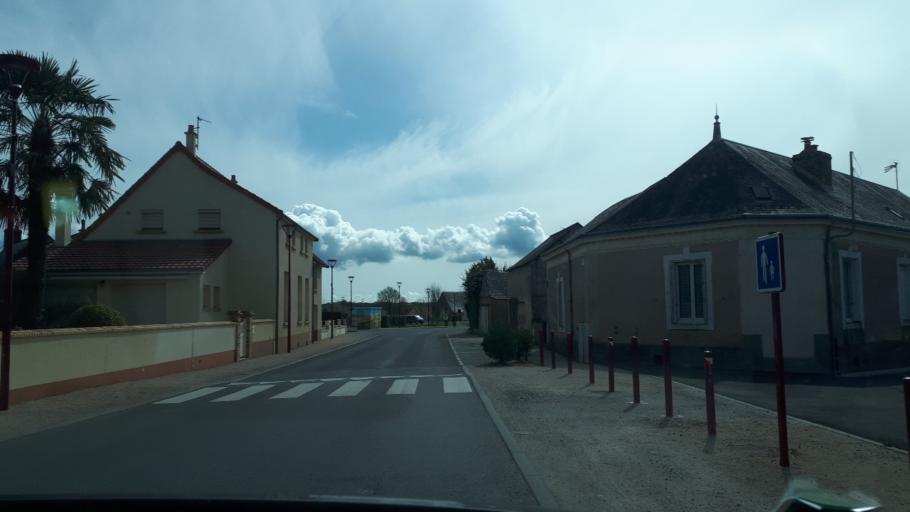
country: FR
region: Pays de la Loire
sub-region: Departement de la Sarthe
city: Saint-Ouen-en-Belin
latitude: 47.8224
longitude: 0.2374
